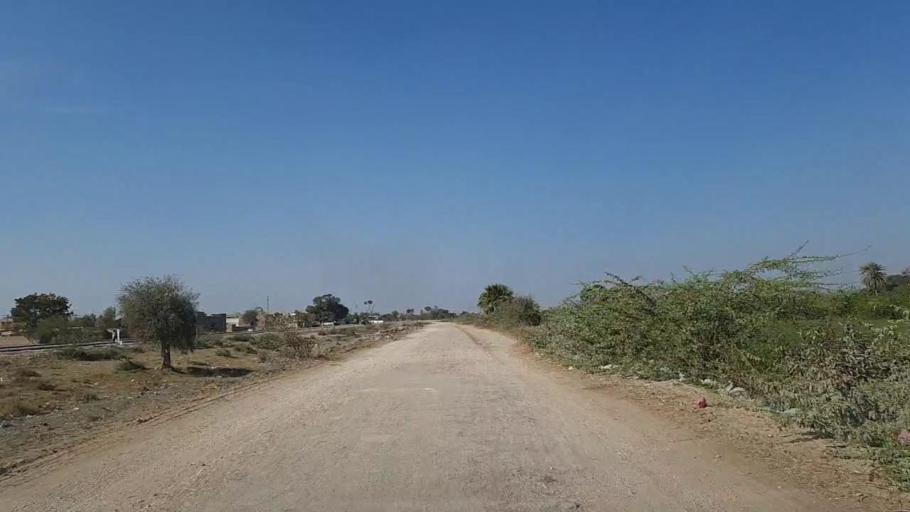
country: PK
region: Sindh
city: Nawabshah
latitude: 26.2254
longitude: 68.4210
